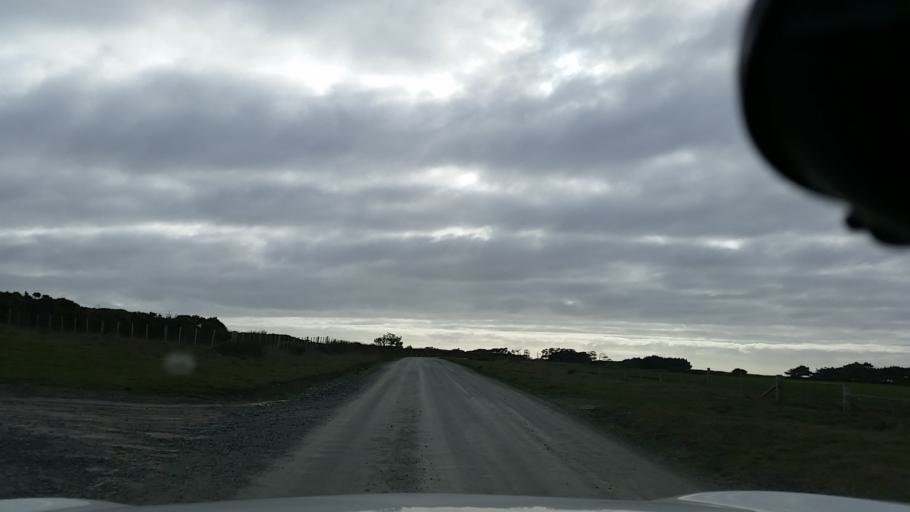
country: NZ
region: Chatham Islands
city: Waitangi
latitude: -43.8472
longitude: -176.5370
